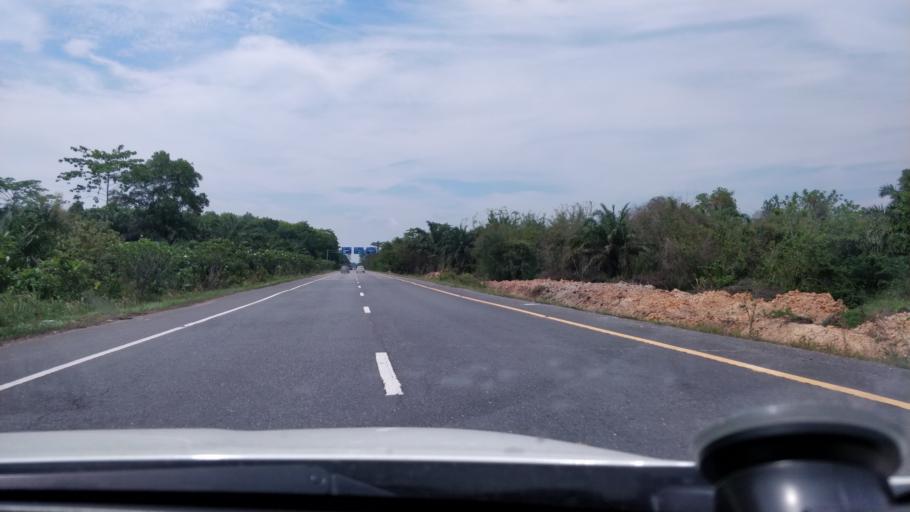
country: TH
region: Surat Thani
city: Khian Sa
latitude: 8.7626
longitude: 99.1610
